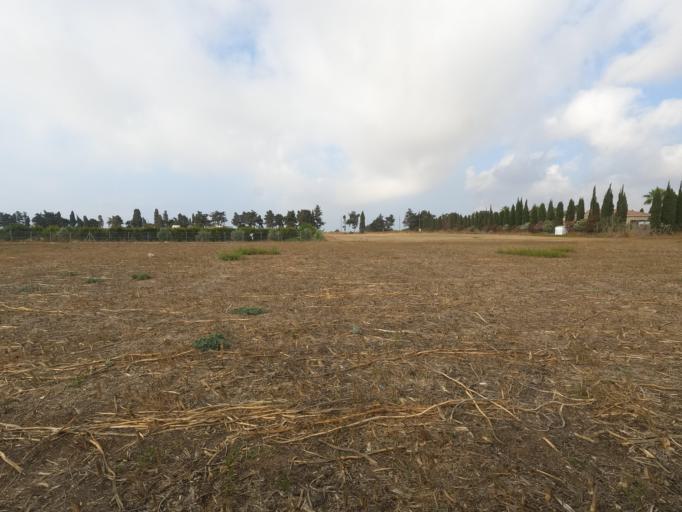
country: CY
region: Larnaka
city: Meneou
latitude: 34.8478
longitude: 33.5967
